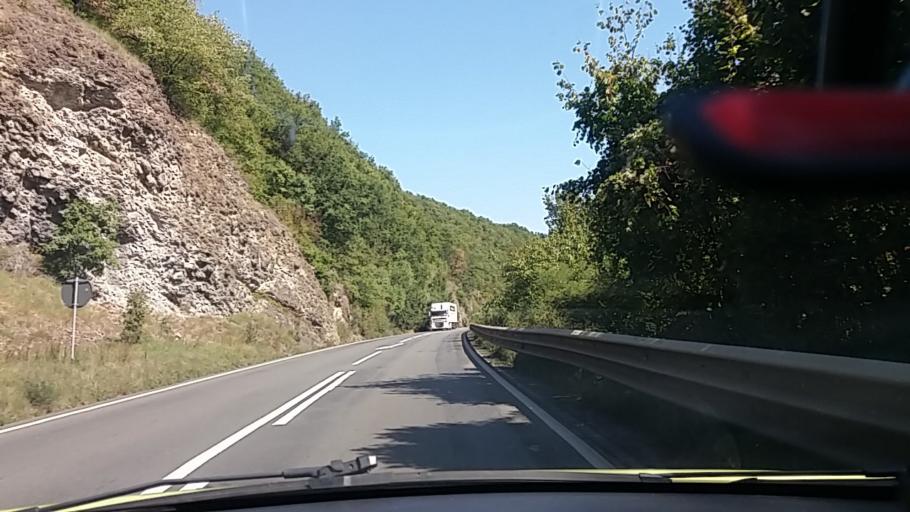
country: RO
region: Arad
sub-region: Comuna Savarsin
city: Savarsin
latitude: 45.9968
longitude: 22.3031
